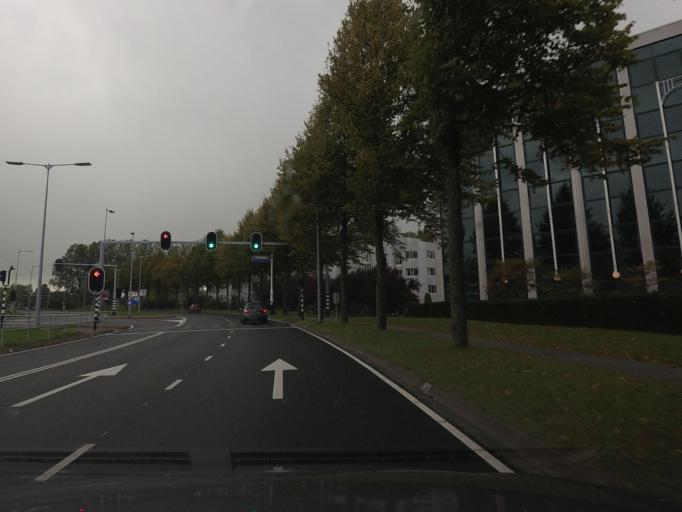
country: NL
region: North Holland
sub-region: Gemeente Haarlemmermeer
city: Hoofddorp
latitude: 52.2941
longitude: 4.6988
